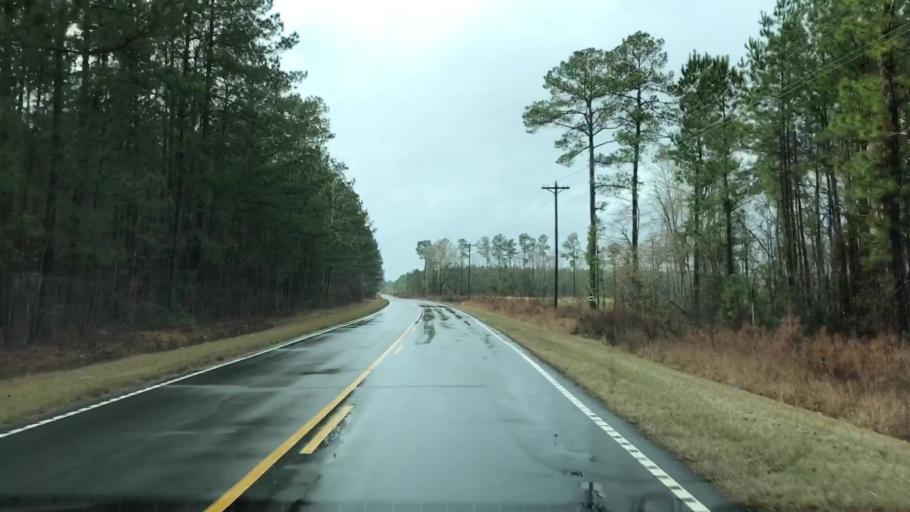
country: US
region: South Carolina
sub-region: Florence County
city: Johnsonville
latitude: 33.6759
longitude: -79.3359
